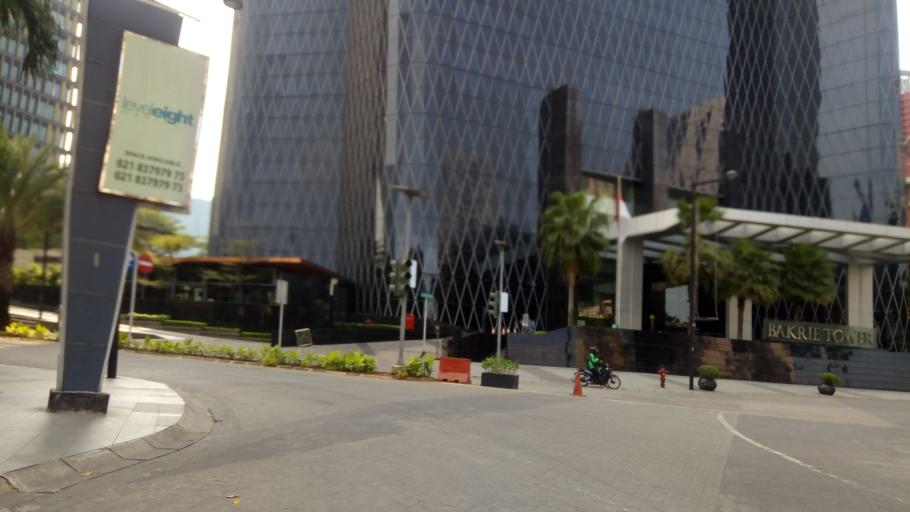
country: ID
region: Jakarta Raya
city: Jakarta
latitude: -6.2198
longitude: 106.8349
